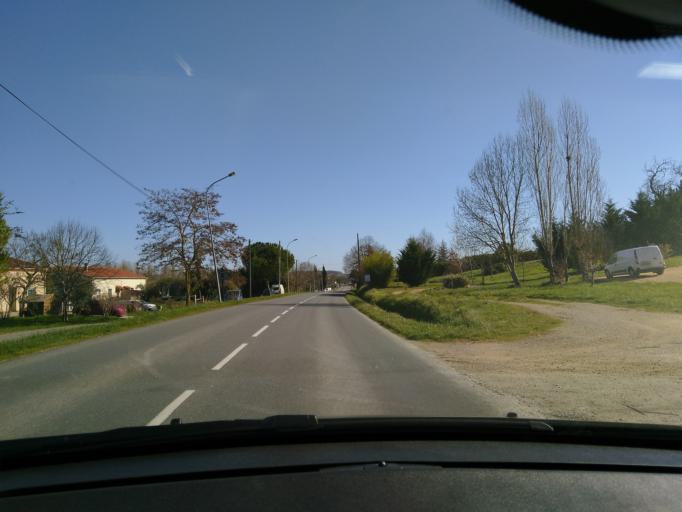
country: FR
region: Aquitaine
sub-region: Departement du Lot-et-Garonne
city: Saint-Hilaire
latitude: 44.5393
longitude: 0.6813
